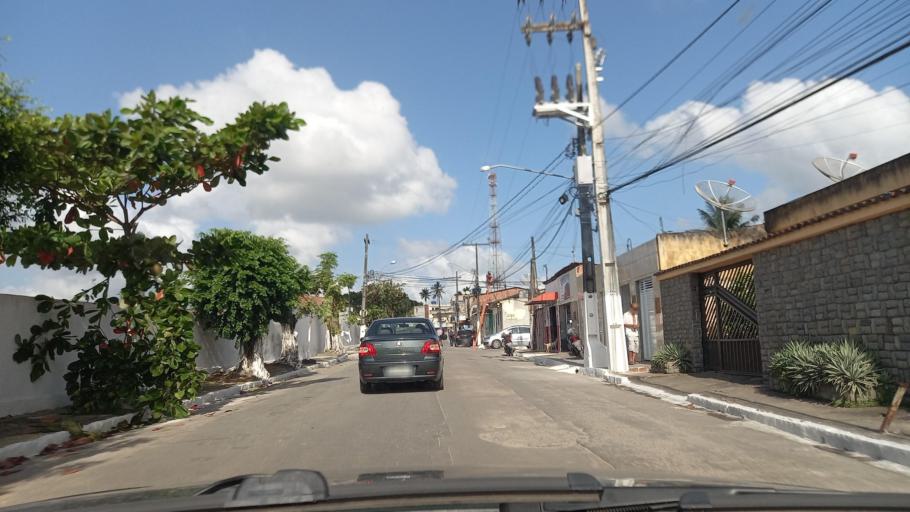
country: BR
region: Pernambuco
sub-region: Goiana
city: Goiana
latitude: -7.5605
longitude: -35.0096
